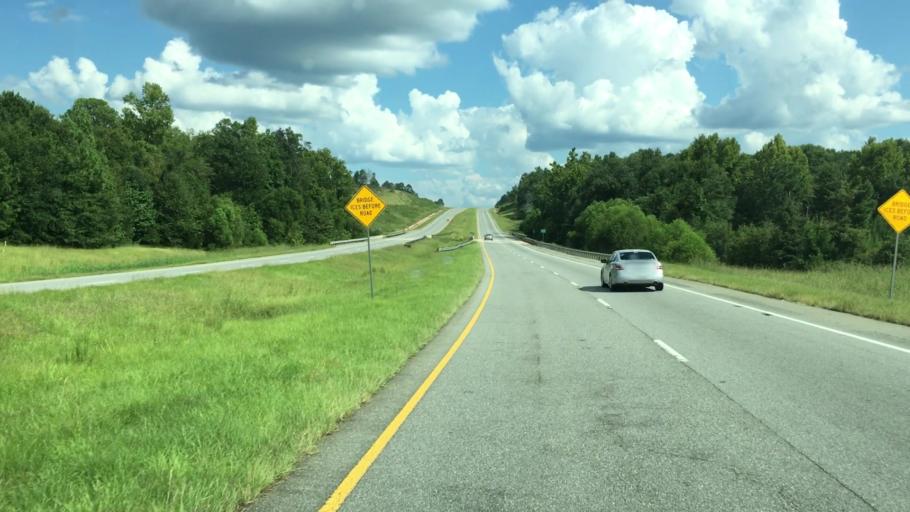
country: US
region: Georgia
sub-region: Wilkinson County
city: Irwinton
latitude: 32.7136
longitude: -83.1399
